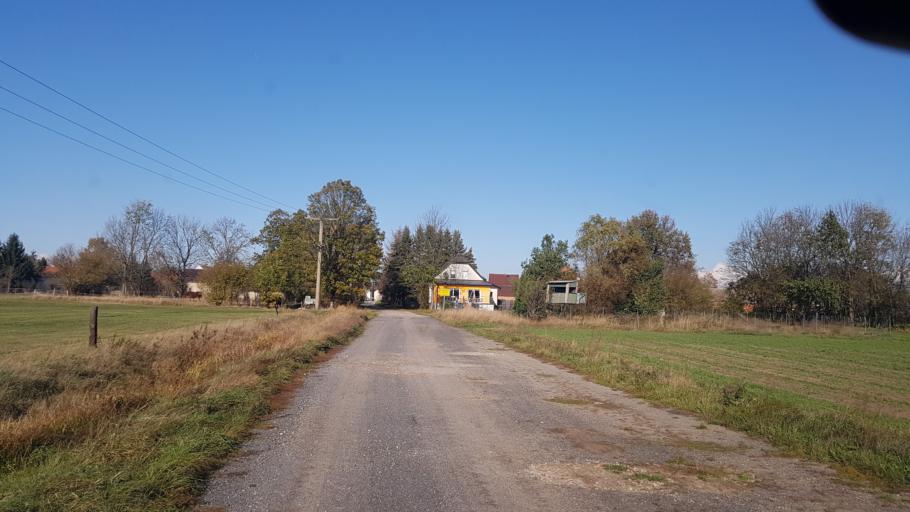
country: DE
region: Brandenburg
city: Ruckersdorf
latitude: 51.5621
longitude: 13.5444
